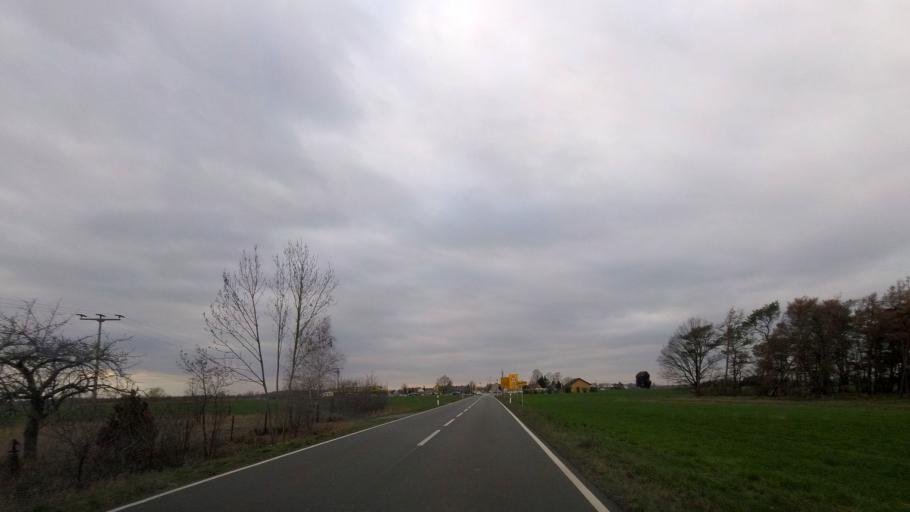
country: DE
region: Saxony-Anhalt
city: Bergwitz
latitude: 51.7903
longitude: 12.6045
